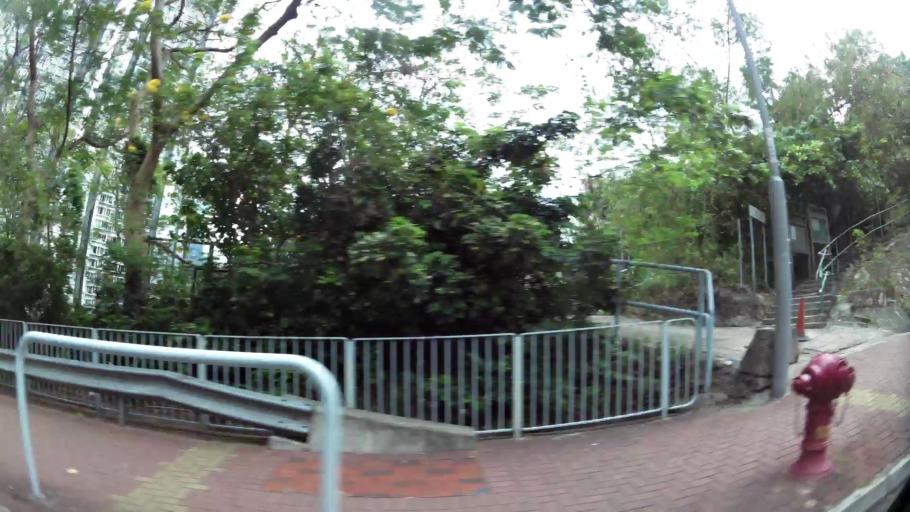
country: HK
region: Tsuen Wan
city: Tsuen Wan
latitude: 22.3763
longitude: 114.1041
